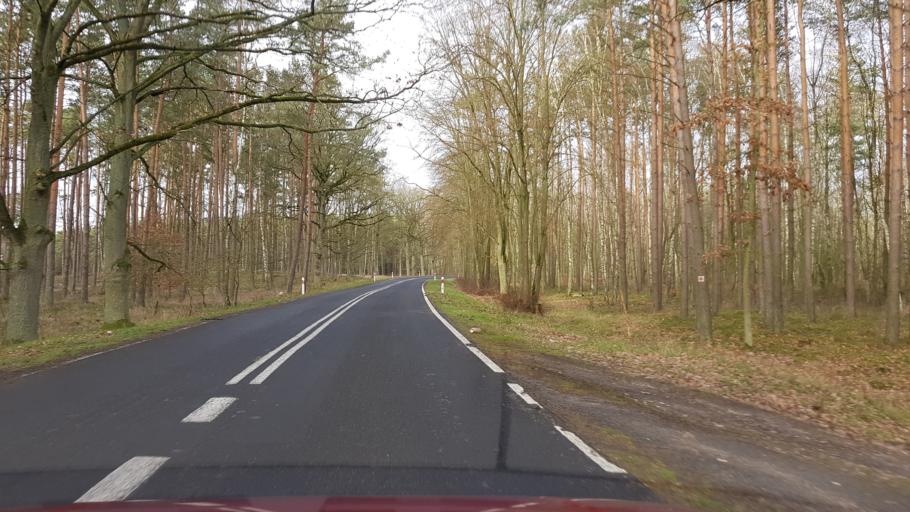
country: PL
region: West Pomeranian Voivodeship
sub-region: Powiat policki
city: Nowe Warpno
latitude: 53.6821
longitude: 14.3551
